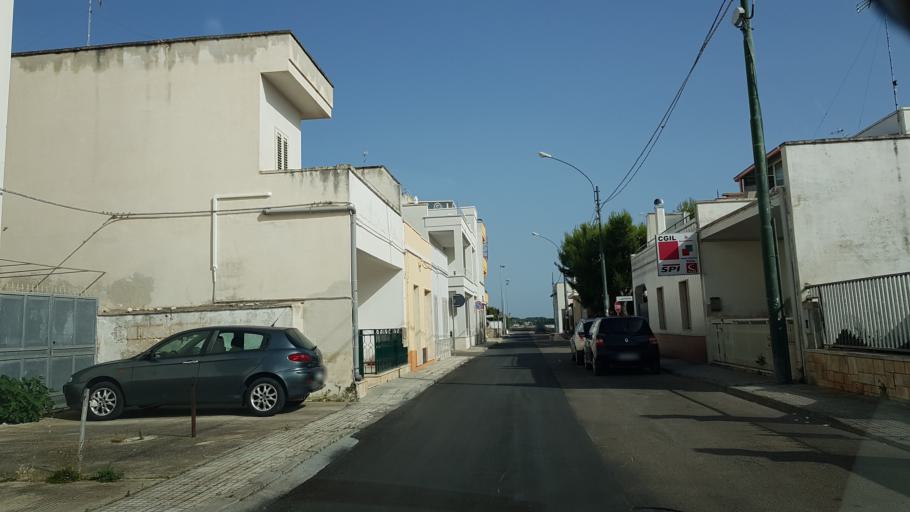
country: IT
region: Apulia
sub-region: Provincia di Lecce
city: Porto Cesareo
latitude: 40.2587
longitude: 17.9023
